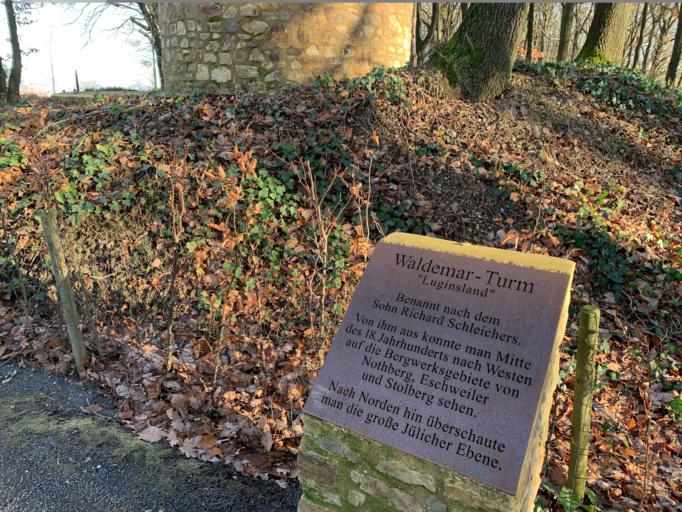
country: DE
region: North Rhine-Westphalia
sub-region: Regierungsbezirk Koln
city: Langerwehe
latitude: 50.8107
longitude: 6.3455
